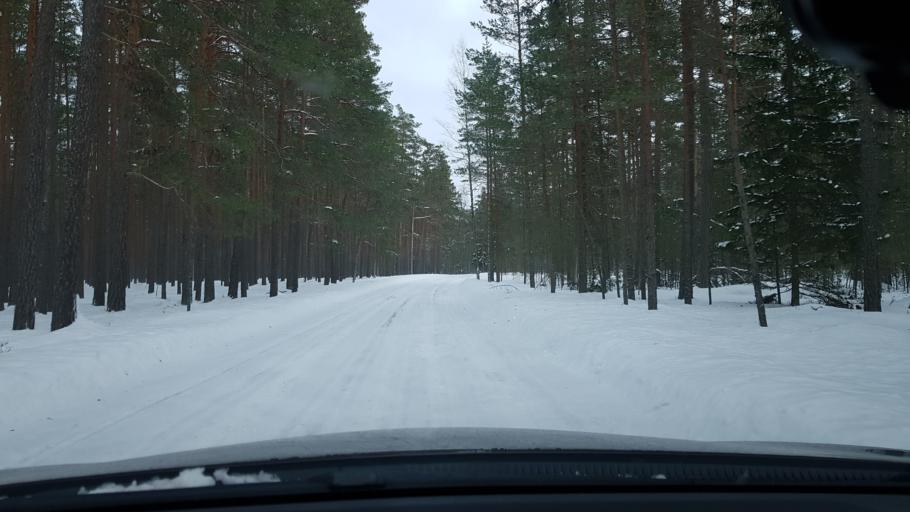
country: EE
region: Laeaene-Virumaa
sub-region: Kadrina vald
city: Kadrina
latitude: 59.5563
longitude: 26.0129
